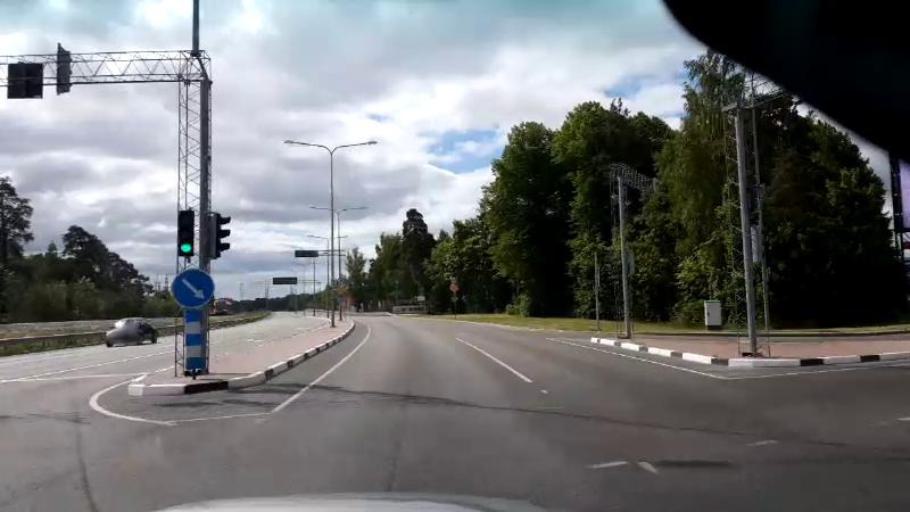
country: EE
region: Paernumaa
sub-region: Paernu linn
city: Parnu
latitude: 58.3720
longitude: 24.5553
